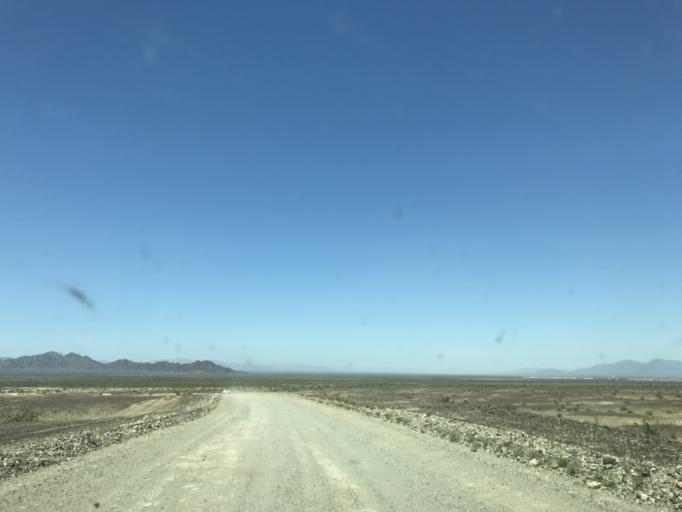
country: US
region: California
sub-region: Riverside County
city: Mesa Verde
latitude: 33.5006
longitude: -114.8525
